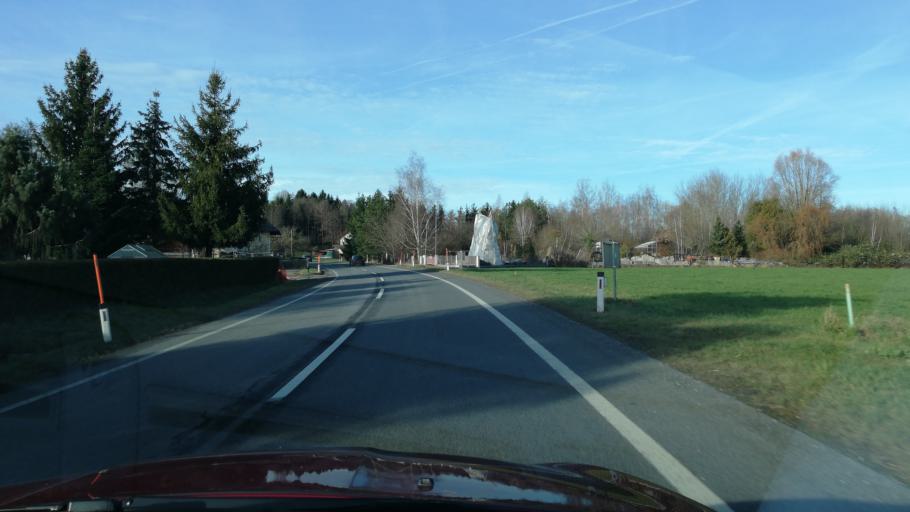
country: AT
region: Upper Austria
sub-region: Politischer Bezirk Kirchdorf an der Krems
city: Micheldorf in Oberoesterreich
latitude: 47.9480
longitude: 14.0981
